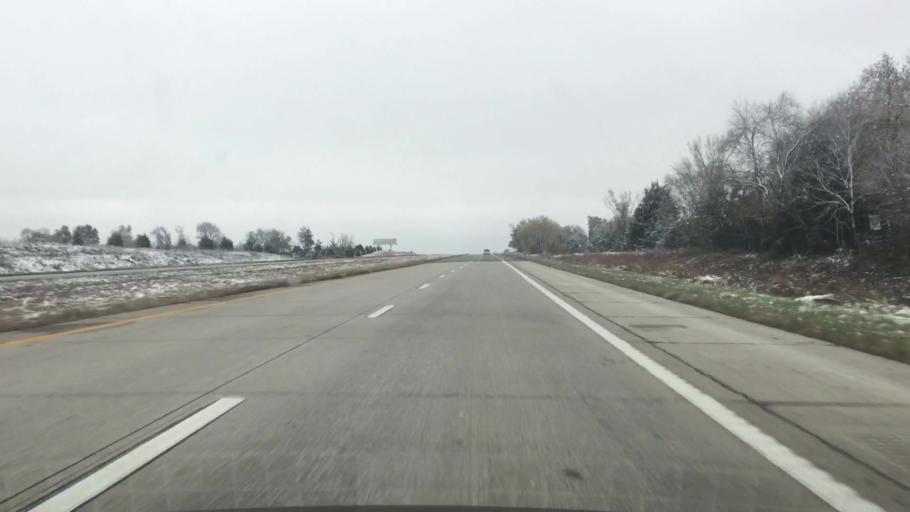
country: US
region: Missouri
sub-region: Saint Clair County
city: Osceola
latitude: 38.1734
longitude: -93.7220
